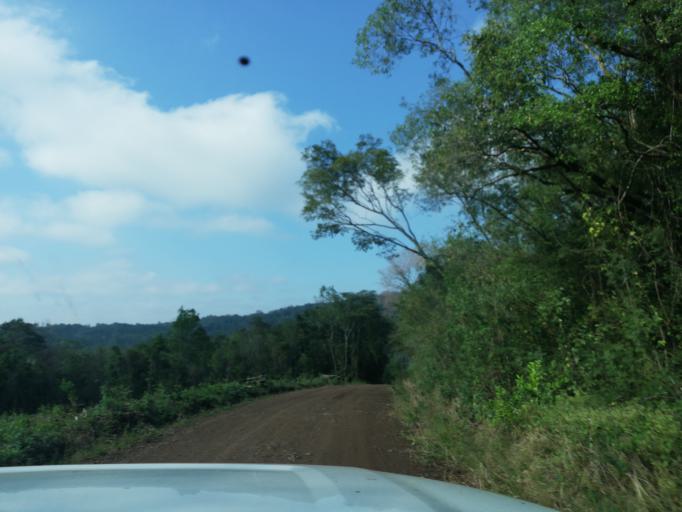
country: AR
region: Misiones
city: Cerro Azul
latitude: -27.6108
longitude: -55.5307
